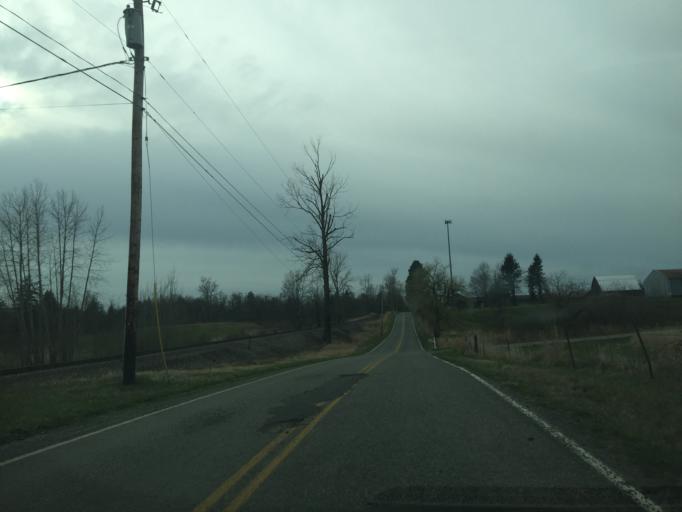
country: US
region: Washington
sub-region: Whatcom County
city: Everson
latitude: 48.9492
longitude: -122.3613
